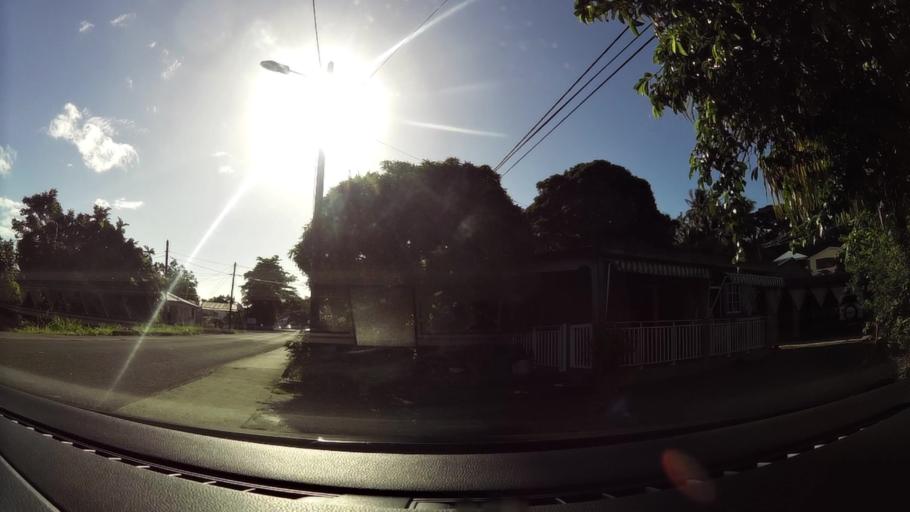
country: GP
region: Guadeloupe
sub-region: Guadeloupe
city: Petit-Canal
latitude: 16.3268
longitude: -61.4478
